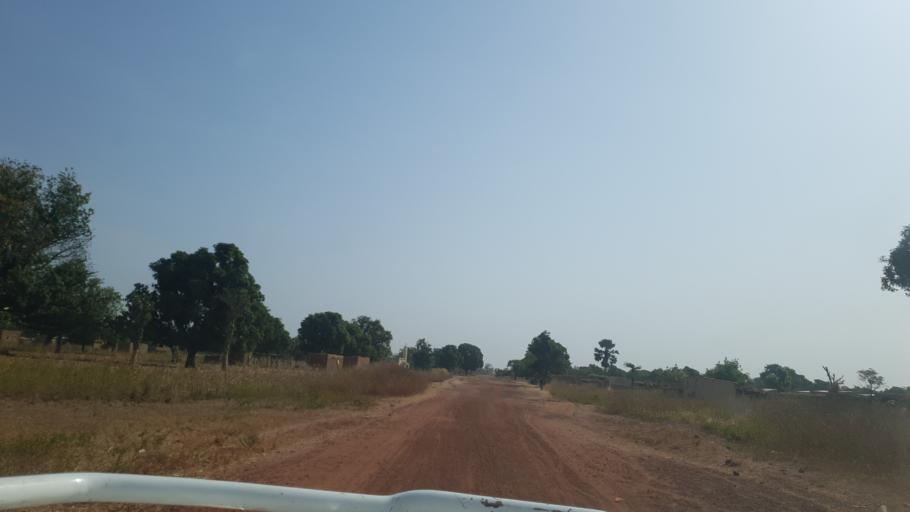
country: ML
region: Koulikoro
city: Dioila
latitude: 12.6688
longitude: -6.6769
